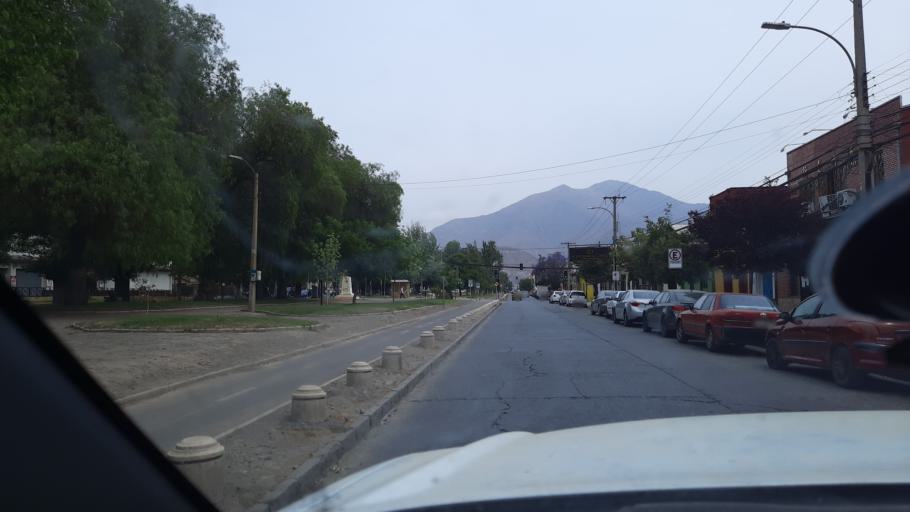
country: CL
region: Valparaiso
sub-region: Provincia de San Felipe
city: San Felipe
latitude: -32.7504
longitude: -70.7201
